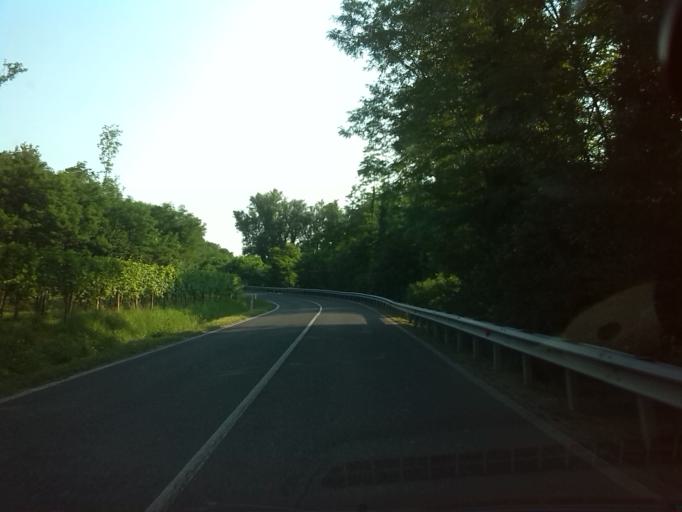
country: IT
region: Friuli Venezia Giulia
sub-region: Provincia di Gorizia
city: Dolegna del Collio
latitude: 46.0136
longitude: 13.4731
